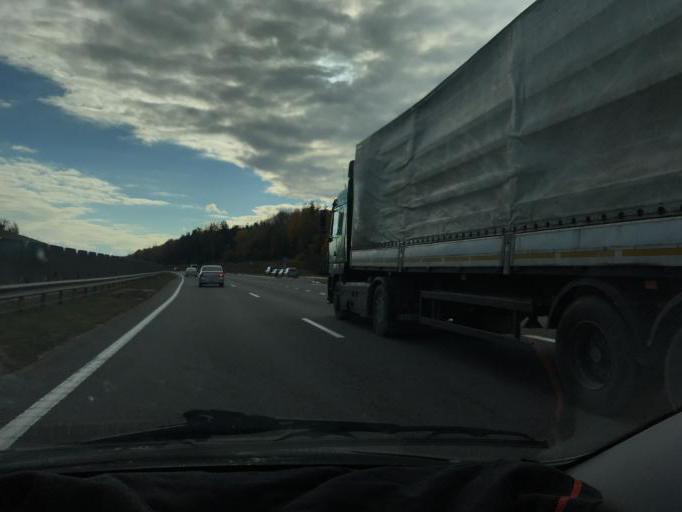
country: BY
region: Minsk
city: Lahoysk
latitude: 54.2041
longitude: 27.8193
